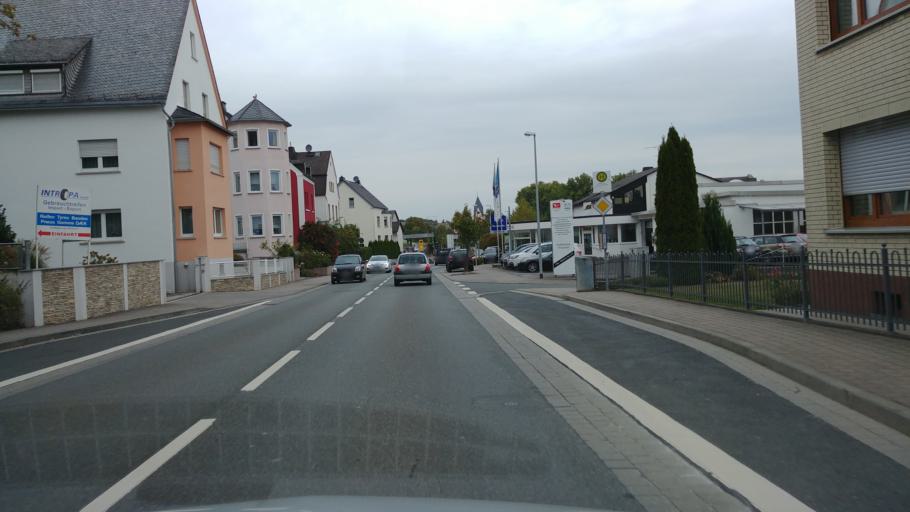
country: DE
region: Rheinland-Pfalz
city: Niederneisen
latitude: 50.3377
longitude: 8.0530
